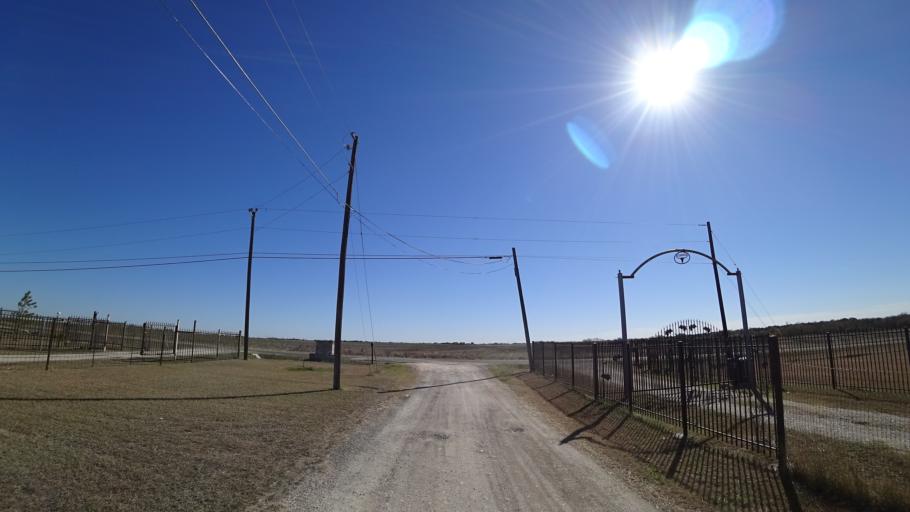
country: US
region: Texas
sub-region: Travis County
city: Garfield
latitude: 30.0966
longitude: -97.6190
